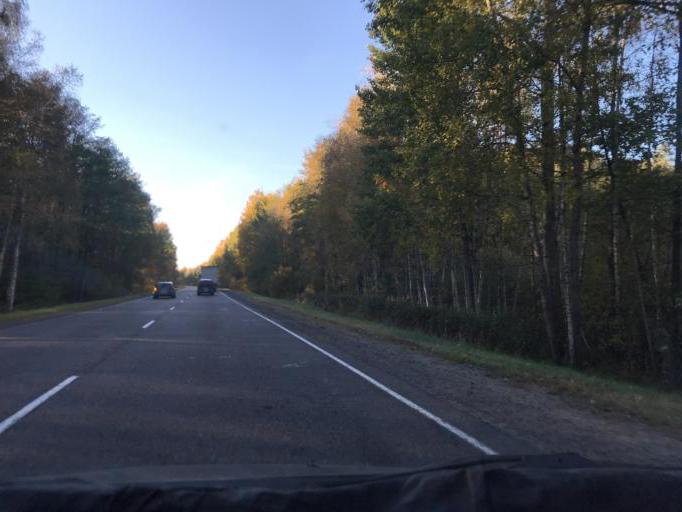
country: BY
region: Gomel
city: Pyetrykaw
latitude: 52.2547
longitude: 28.3527
